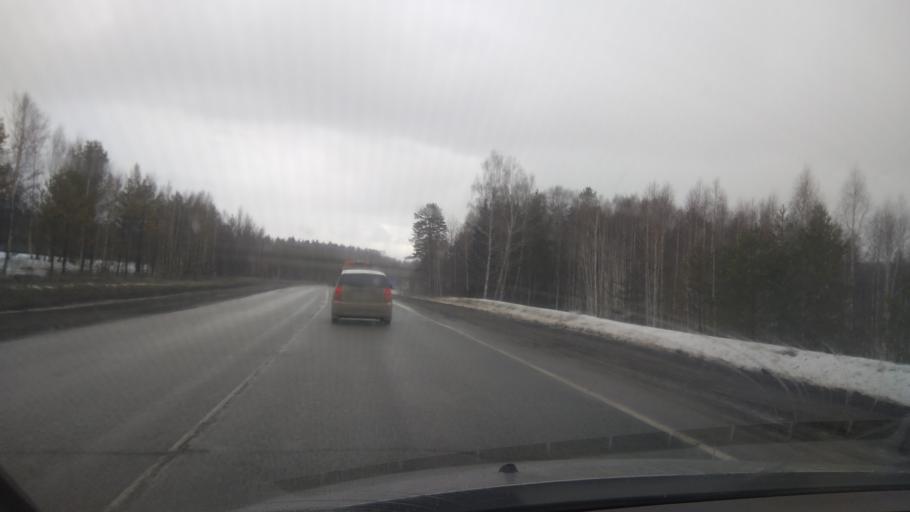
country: RU
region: Sverdlovsk
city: Ufimskiy
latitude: 56.7793
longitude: 58.2591
